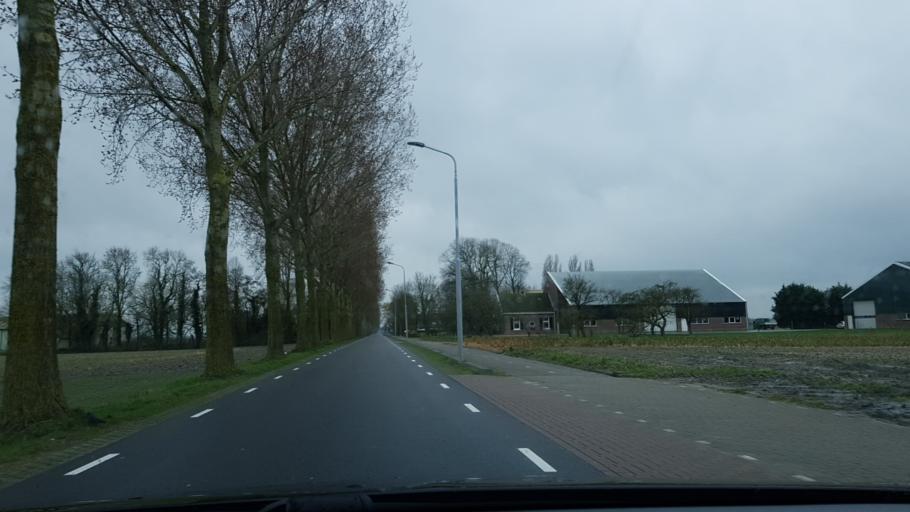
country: NL
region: North Holland
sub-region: Gemeente Haarlemmermeer
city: Hoofddorp
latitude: 52.2712
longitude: 4.6832
